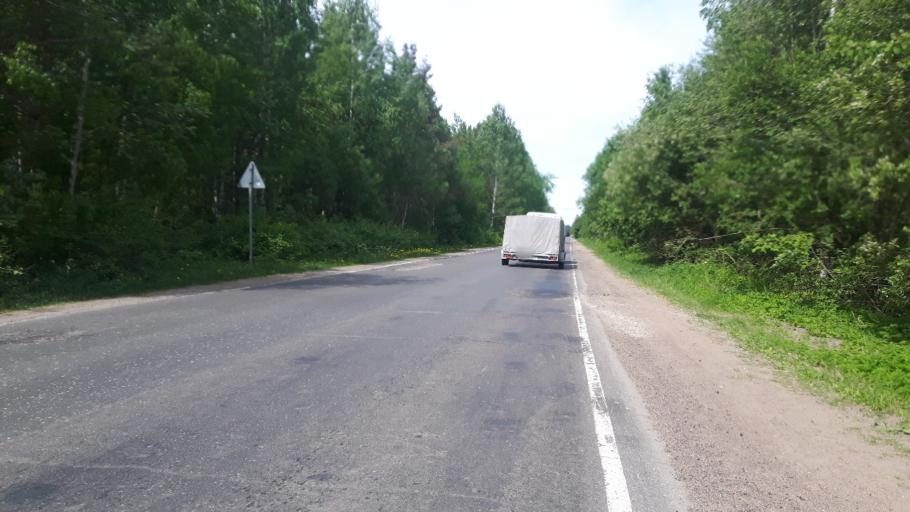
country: RU
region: Leningrad
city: Ust'-Luga
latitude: 59.6407
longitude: 28.2772
